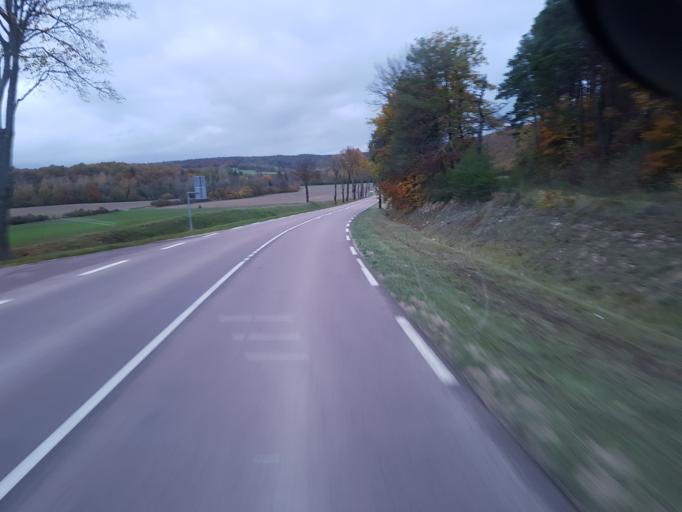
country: FR
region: Champagne-Ardenne
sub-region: Departement de l'Aube
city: Mussy-sur-Seine
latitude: 48.0018
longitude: 4.4744
